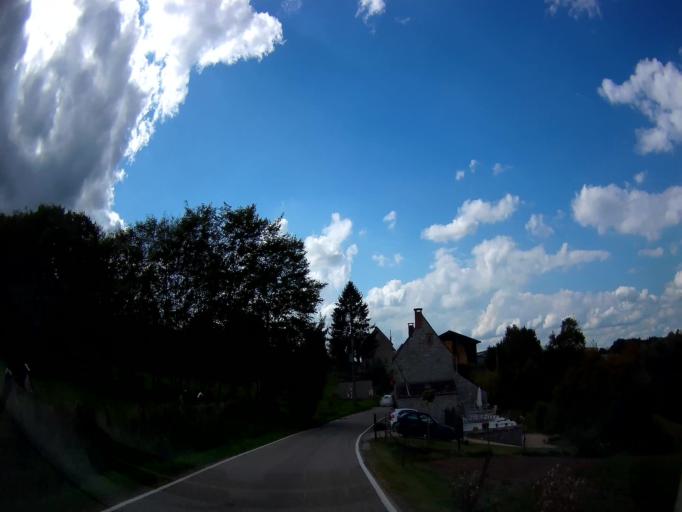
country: BE
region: Wallonia
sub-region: Province de Namur
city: Assesse
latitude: 50.3541
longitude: 4.9708
